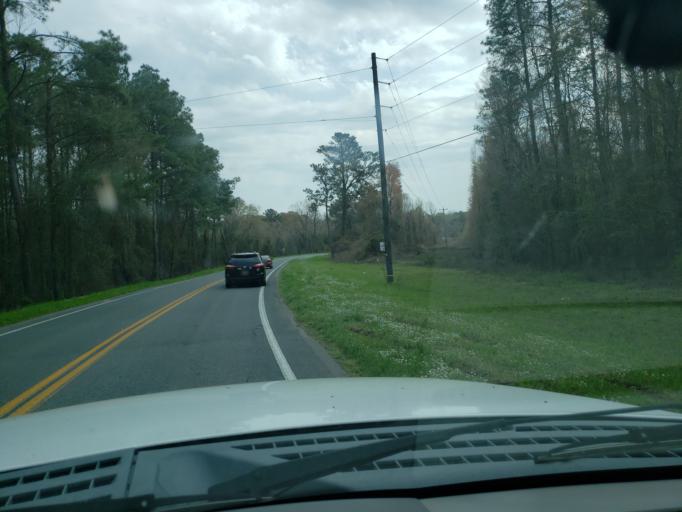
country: US
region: North Carolina
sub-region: Duplin County
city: Beulaville
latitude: 34.7881
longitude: -77.8386
